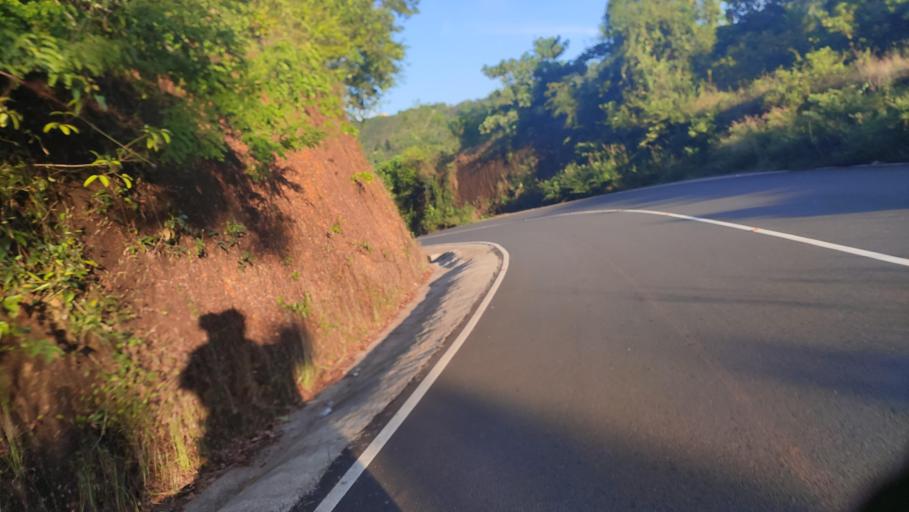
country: IN
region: Kerala
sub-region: Kasaragod District
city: Kasaragod
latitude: 12.4630
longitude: 75.0871
